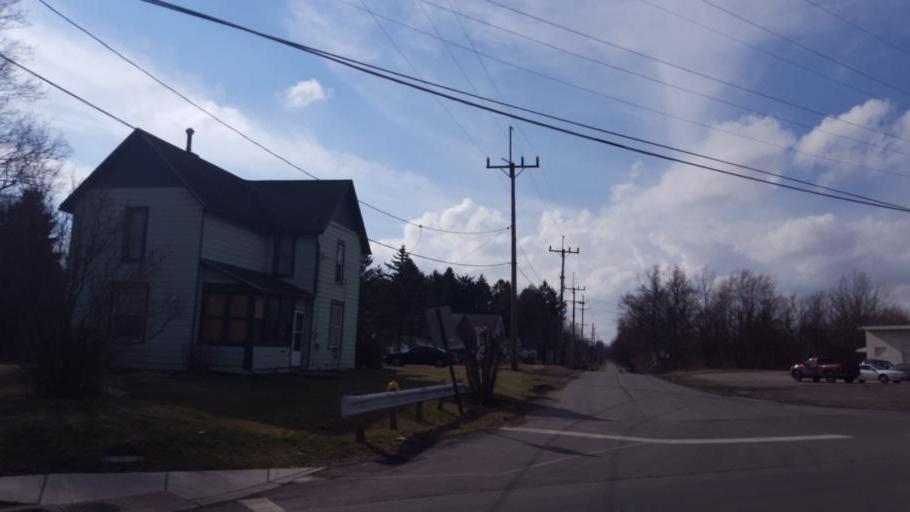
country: US
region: Ohio
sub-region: Richland County
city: Mansfield
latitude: 40.7729
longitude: -82.5295
